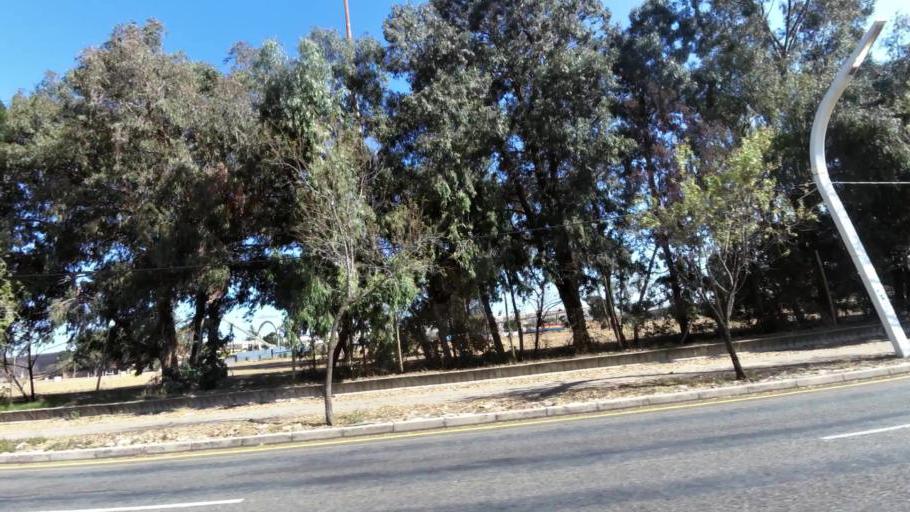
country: ZA
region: Gauteng
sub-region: City of Johannesburg Metropolitan Municipality
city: Johannesburg
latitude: -26.2403
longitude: 27.9855
